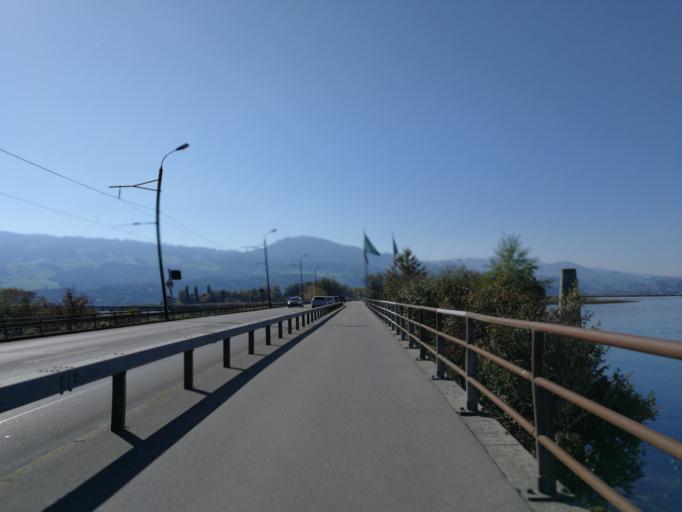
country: CH
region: Saint Gallen
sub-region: Wahlkreis See-Gaster
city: Rapperswil
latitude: 47.2203
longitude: 8.8093
